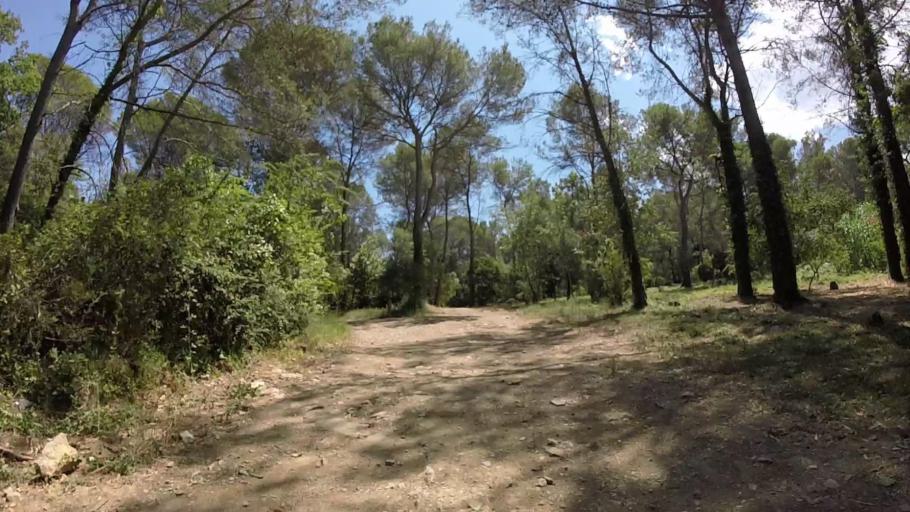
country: FR
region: Provence-Alpes-Cote d'Azur
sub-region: Departement des Alpes-Maritimes
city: Mougins
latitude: 43.5984
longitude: 7.0161
